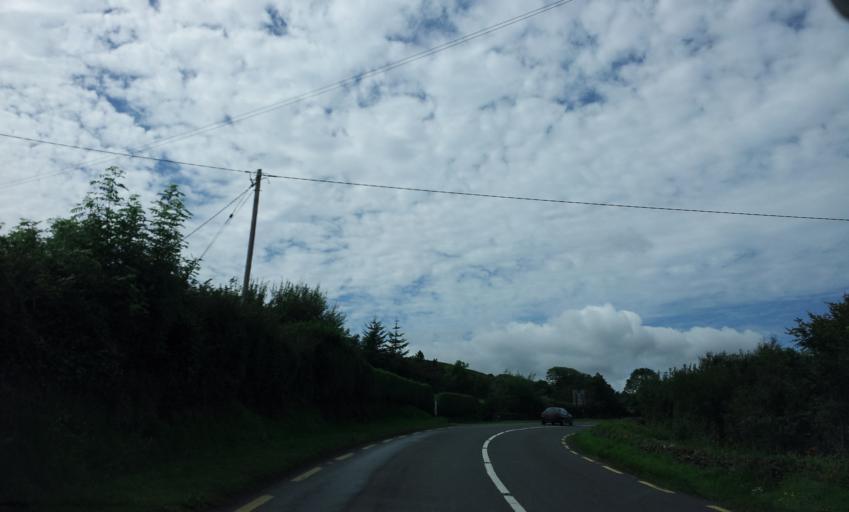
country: IE
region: Munster
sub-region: Ciarrai
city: Killorglin
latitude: 52.0603
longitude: -9.9233
